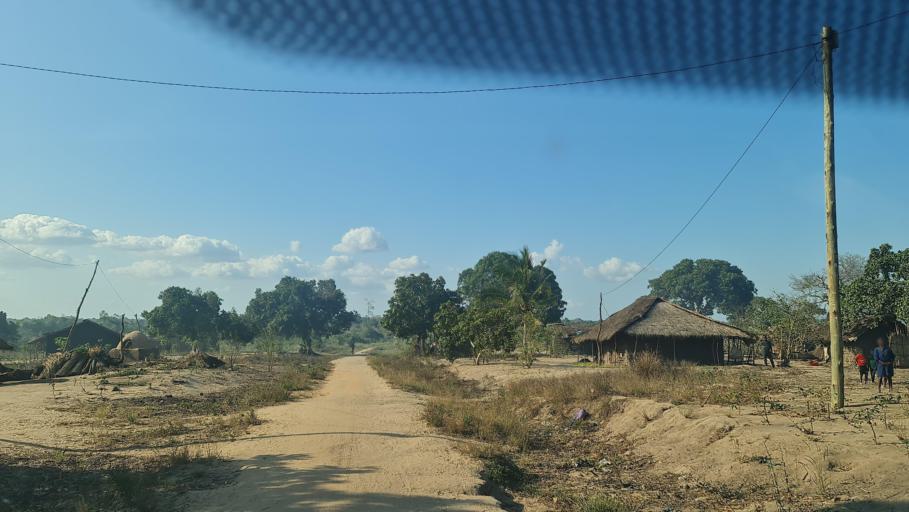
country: MZ
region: Nampula
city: Ilha de Mocambique
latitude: -15.0168
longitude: 40.5601
